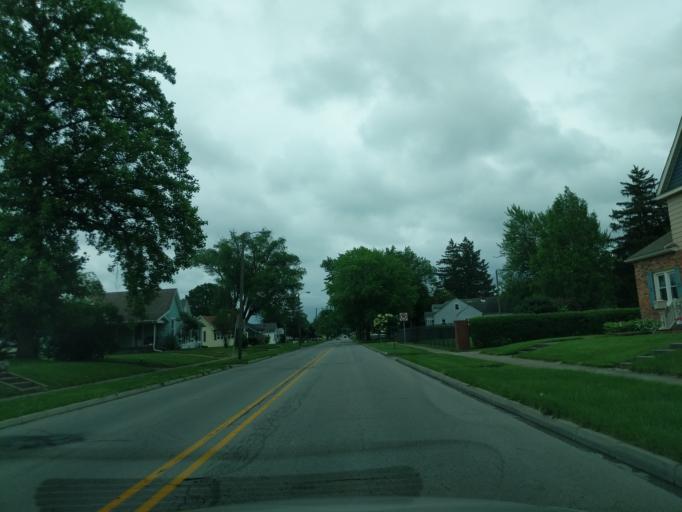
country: US
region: Indiana
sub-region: Madison County
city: Elwood
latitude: 40.2769
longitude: -85.8551
